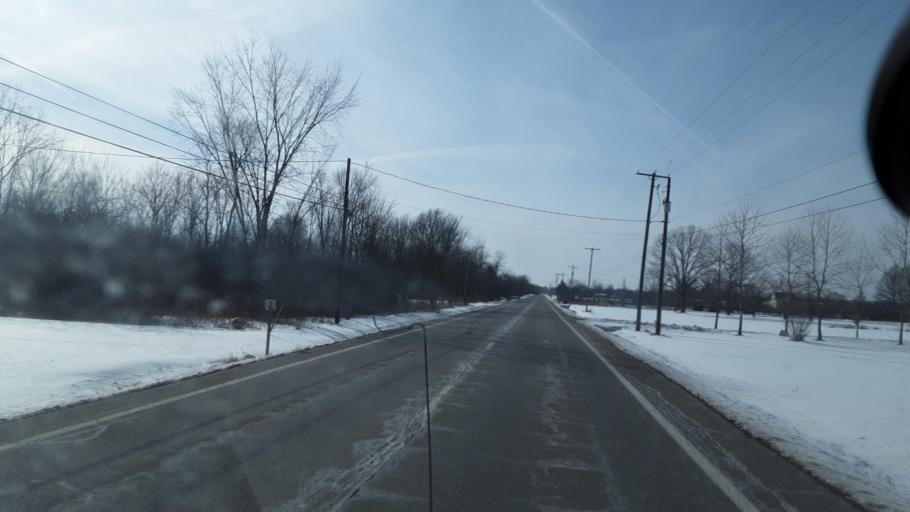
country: US
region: Ohio
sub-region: Mahoning County
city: Craig Beach
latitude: 41.0245
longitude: -80.9643
